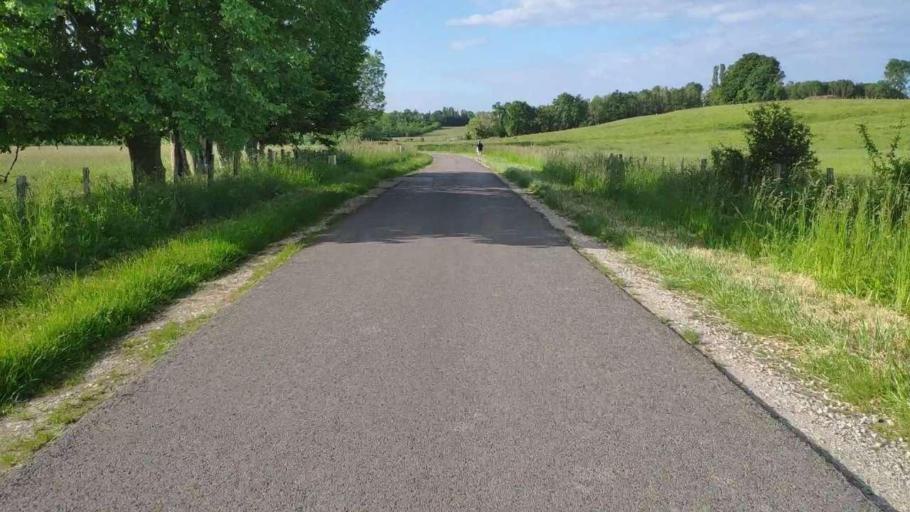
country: FR
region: Franche-Comte
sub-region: Departement du Jura
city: Bletterans
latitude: 46.7564
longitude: 5.4484
